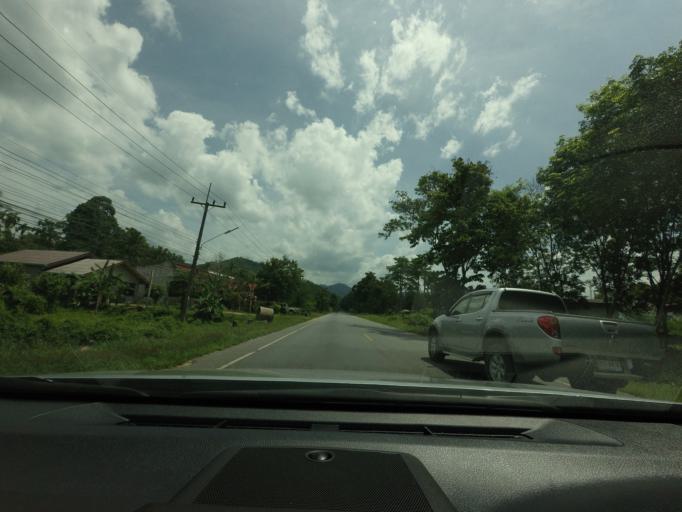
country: TH
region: Yala
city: Raman
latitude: 6.4547
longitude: 101.3525
